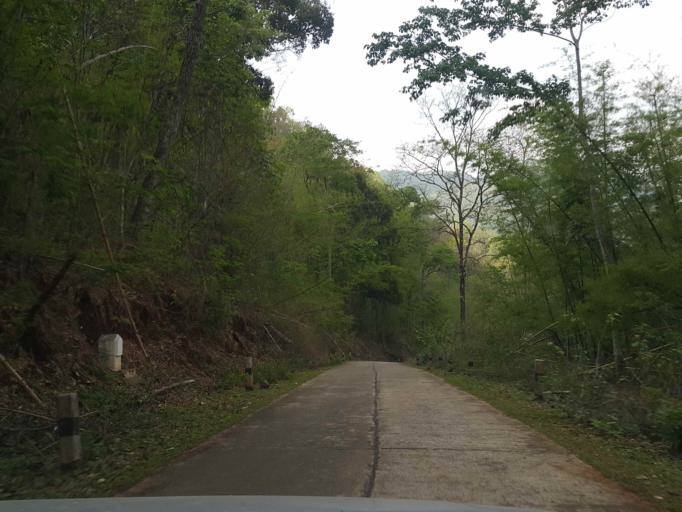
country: TH
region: Chiang Mai
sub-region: Amphoe Chiang Dao
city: Chiang Dao
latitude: 19.3912
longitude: 98.7691
